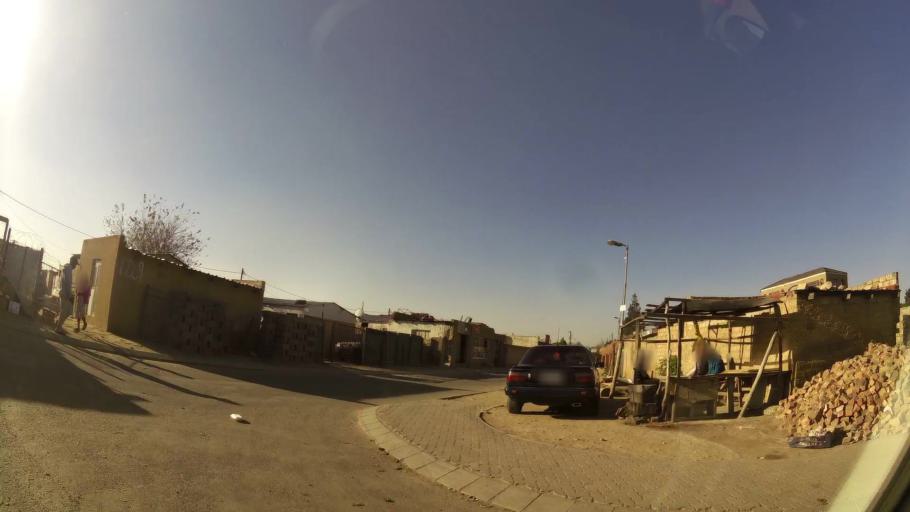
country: ZA
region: Gauteng
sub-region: City of Johannesburg Metropolitan Municipality
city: Diepsloot
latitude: -25.9262
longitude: 28.0046
